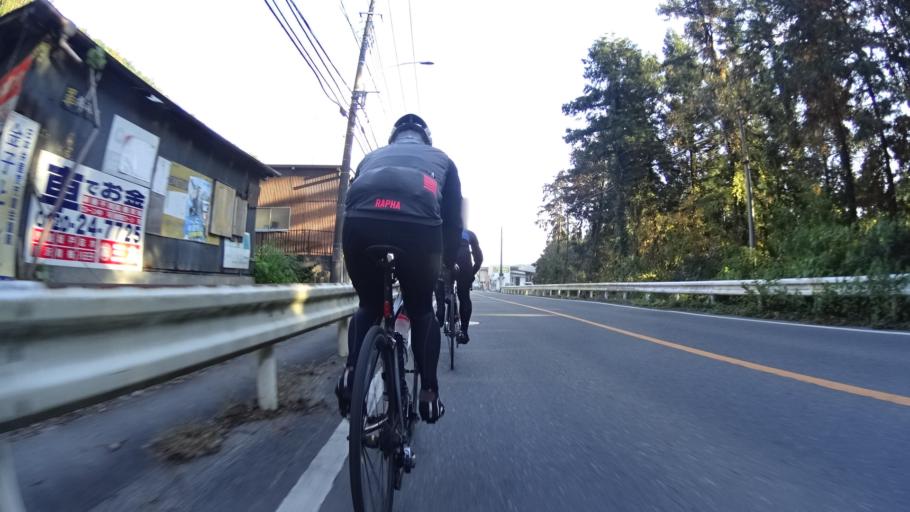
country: JP
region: Saitama
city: Hanno
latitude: 35.8669
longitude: 139.2840
